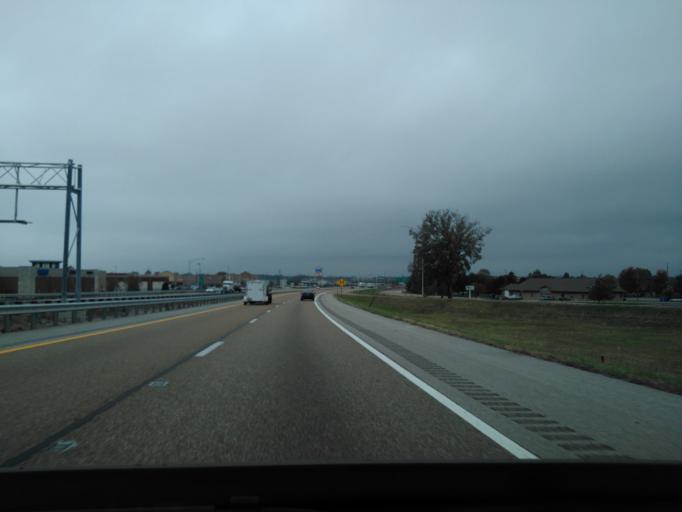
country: US
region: Illinois
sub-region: Madison County
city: Collinsville
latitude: 38.6787
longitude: -90.0143
